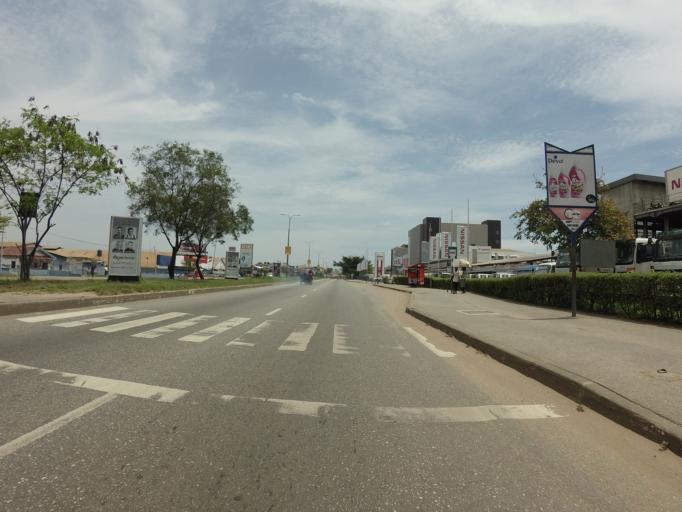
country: GH
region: Greater Accra
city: Accra
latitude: 5.5591
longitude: -0.2256
